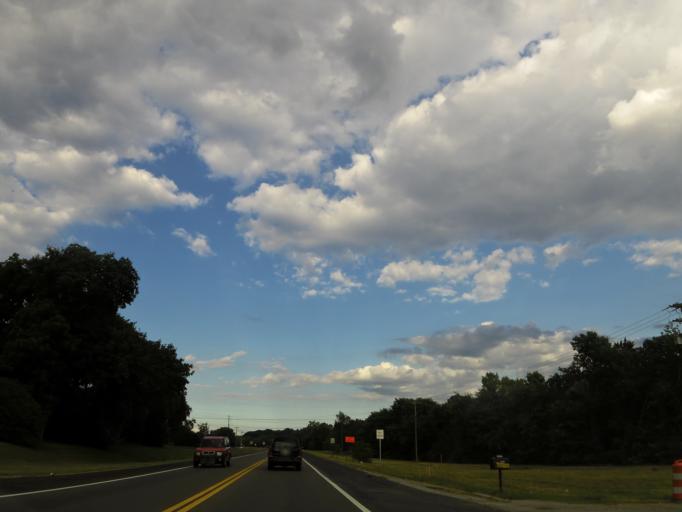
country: US
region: Tennessee
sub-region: Maury County
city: Columbia
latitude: 35.6362
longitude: -86.9910
